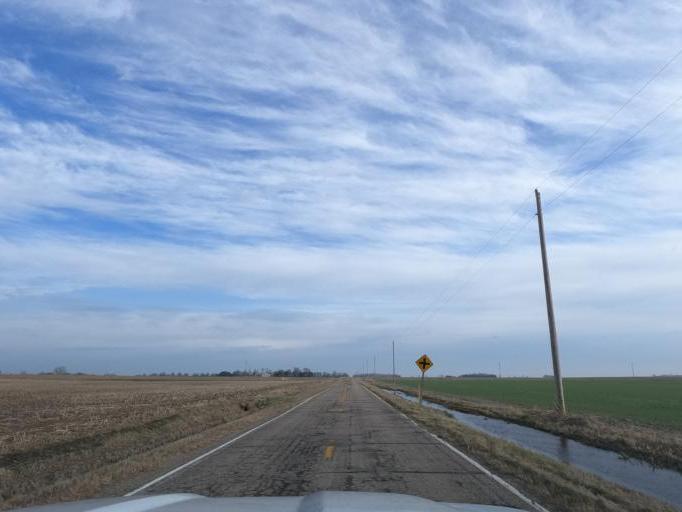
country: US
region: Kansas
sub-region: Rice County
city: Sterling
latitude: 38.0991
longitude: -98.2522
